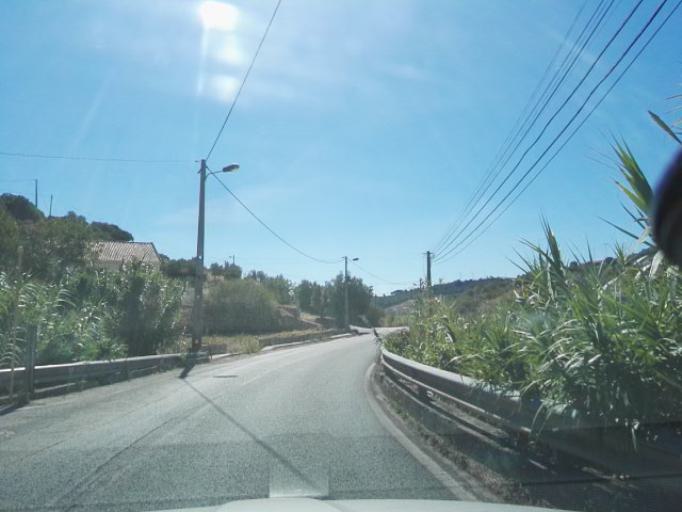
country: PT
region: Lisbon
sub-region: Vila Franca de Xira
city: Sao Joao dos Montes
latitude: 38.9401
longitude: -9.0286
